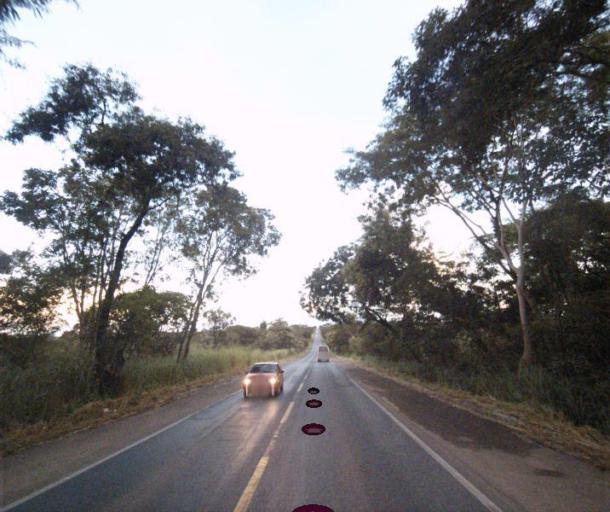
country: BR
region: Goias
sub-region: Uruacu
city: Uruacu
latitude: -14.4131
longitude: -49.1573
